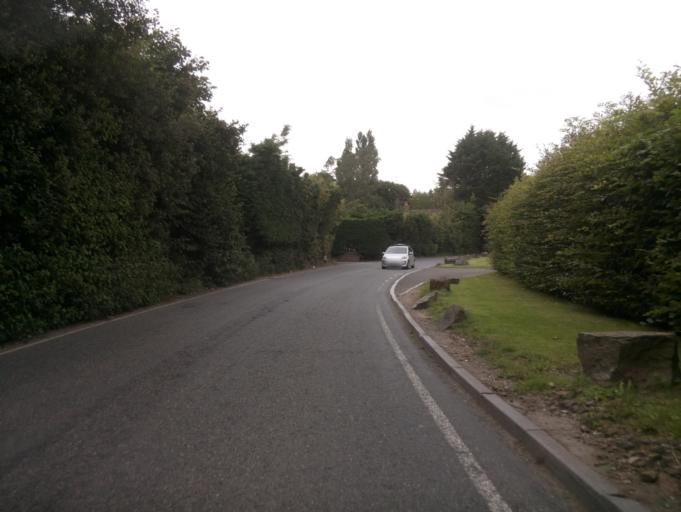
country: GB
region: England
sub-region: North Somerset
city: Churchill
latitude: 51.3460
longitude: -2.7837
